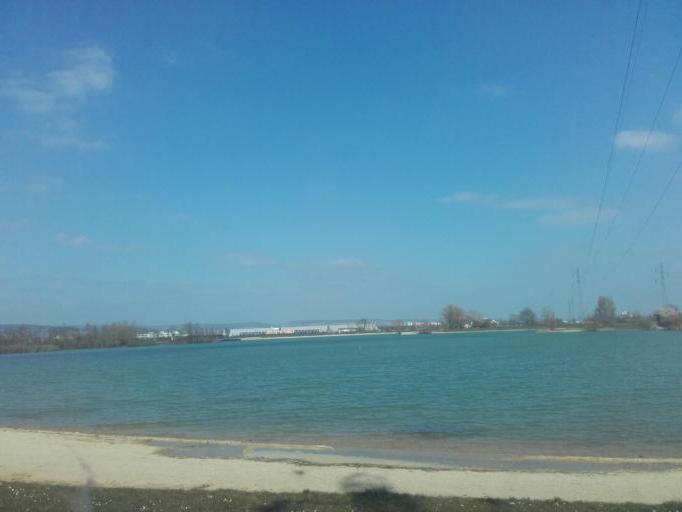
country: FR
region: Bourgogne
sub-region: Departement de la Cote-d'Or
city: Bligny-les-Beaune
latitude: 46.9937
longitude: 4.8414
